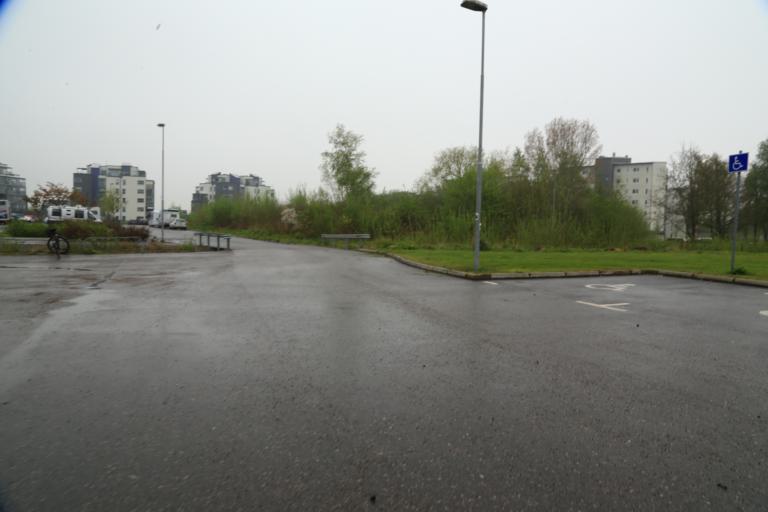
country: SE
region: Halland
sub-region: Varbergs Kommun
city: Traslovslage
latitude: 57.0893
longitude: 12.2762
